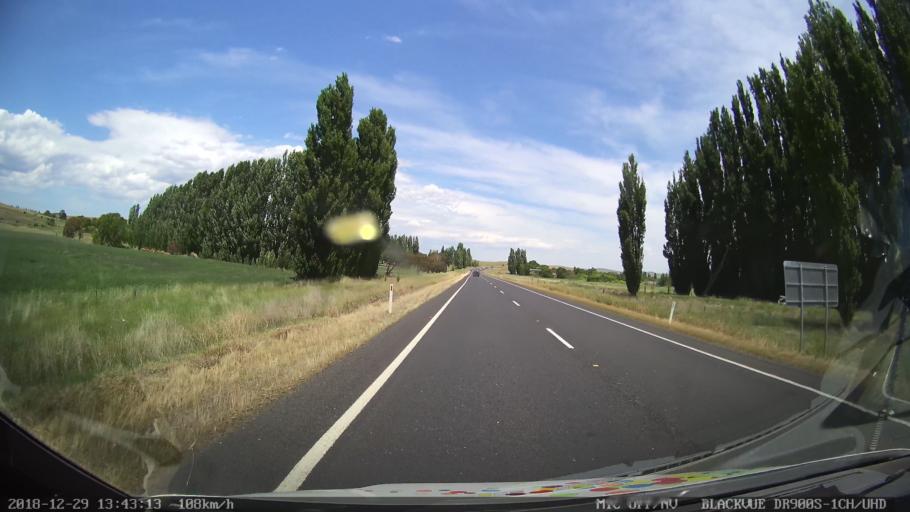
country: AU
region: New South Wales
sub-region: Cooma-Monaro
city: Cooma
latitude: -36.0690
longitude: 149.1588
